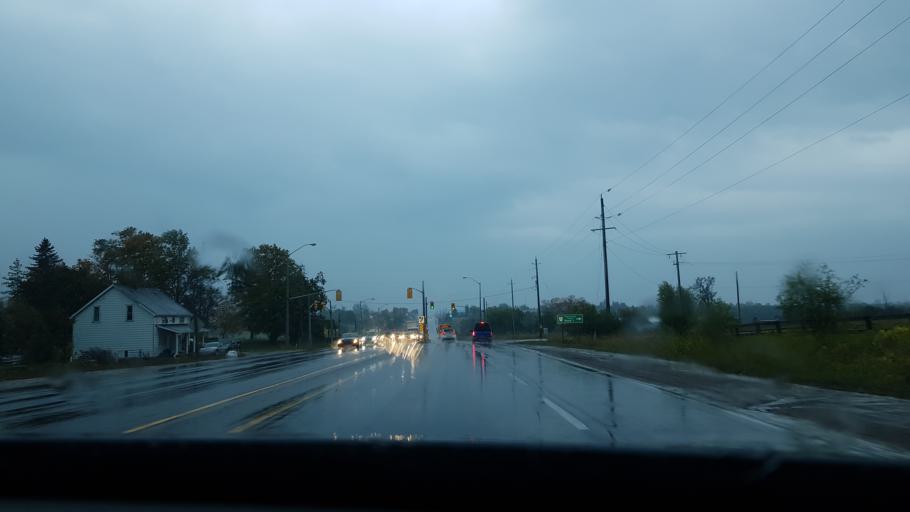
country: CA
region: Ontario
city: Peterborough
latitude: 44.3505
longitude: -78.3632
